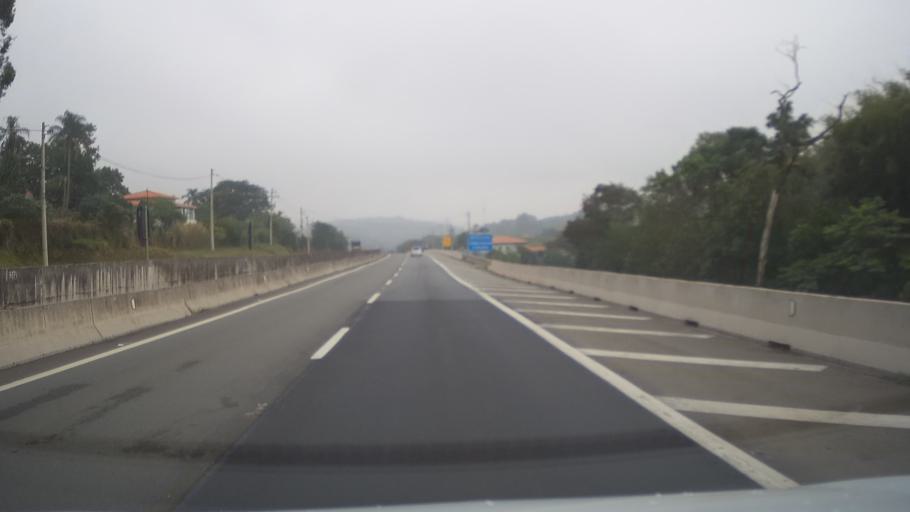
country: BR
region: Sao Paulo
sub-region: Itatiba
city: Itatiba
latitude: -23.0920
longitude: -46.8477
